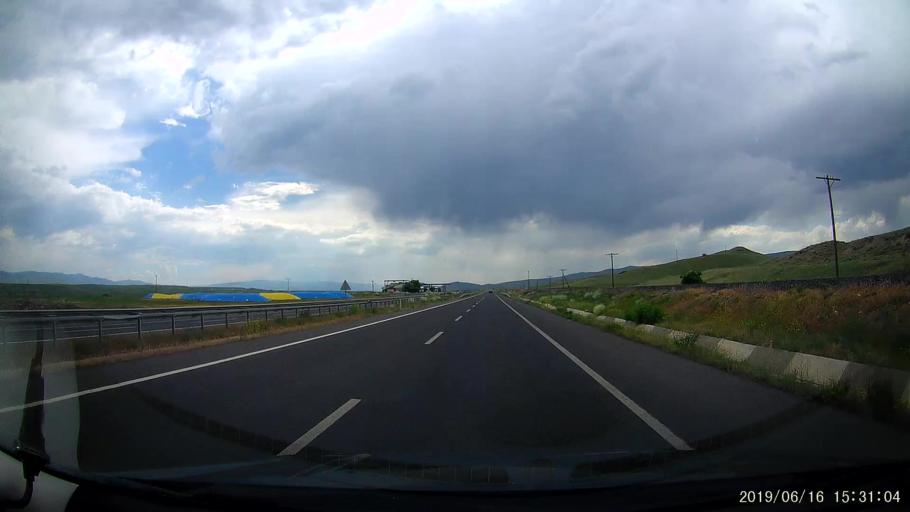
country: TR
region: Erzurum
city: Horasan
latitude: 40.0340
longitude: 42.0882
